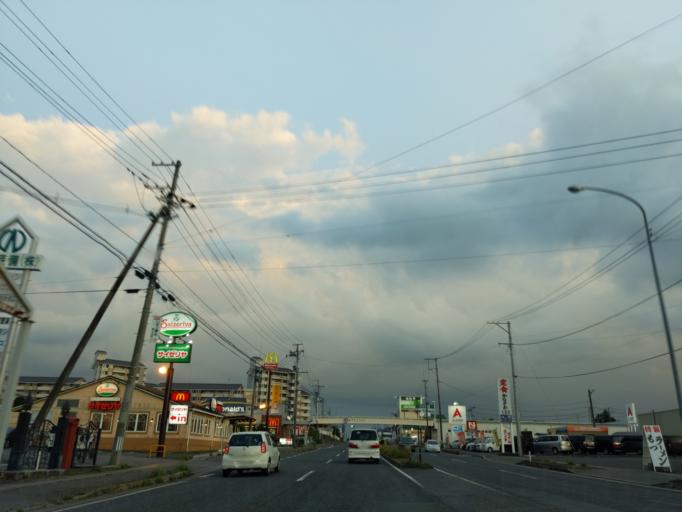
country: JP
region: Fukushima
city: Sukagawa
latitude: 37.3122
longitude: 140.3656
